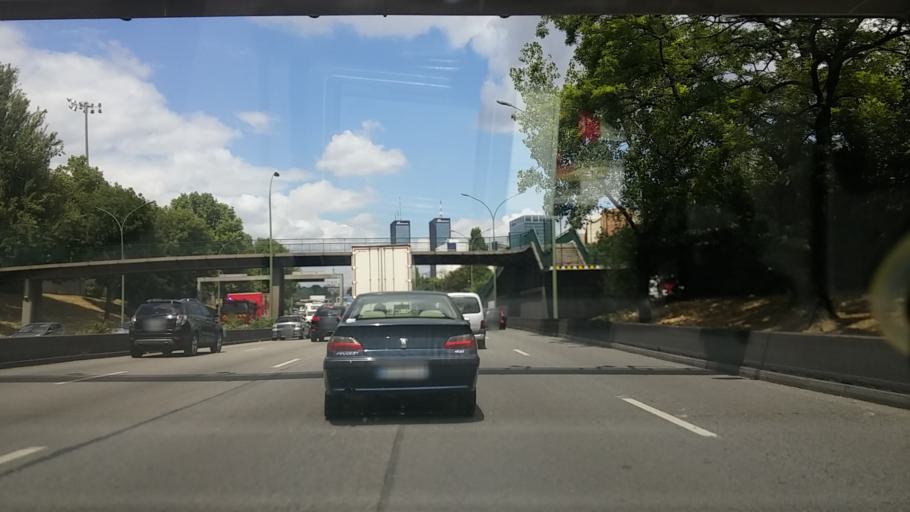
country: FR
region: Ile-de-France
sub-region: Departement de Seine-Saint-Denis
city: Bagnolet
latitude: 48.8572
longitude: 2.4142
